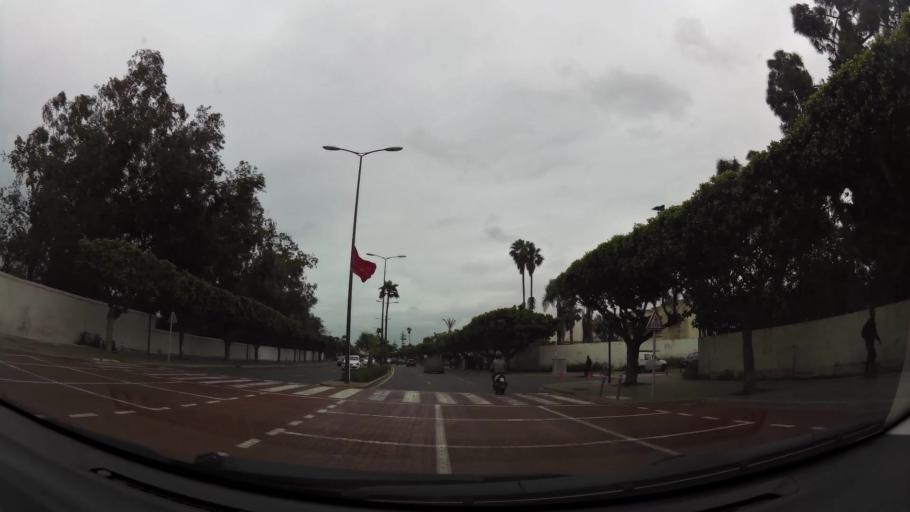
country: MA
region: Grand Casablanca
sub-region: Casablanca
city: Casablanca
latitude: 33.5837
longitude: -7.6575
